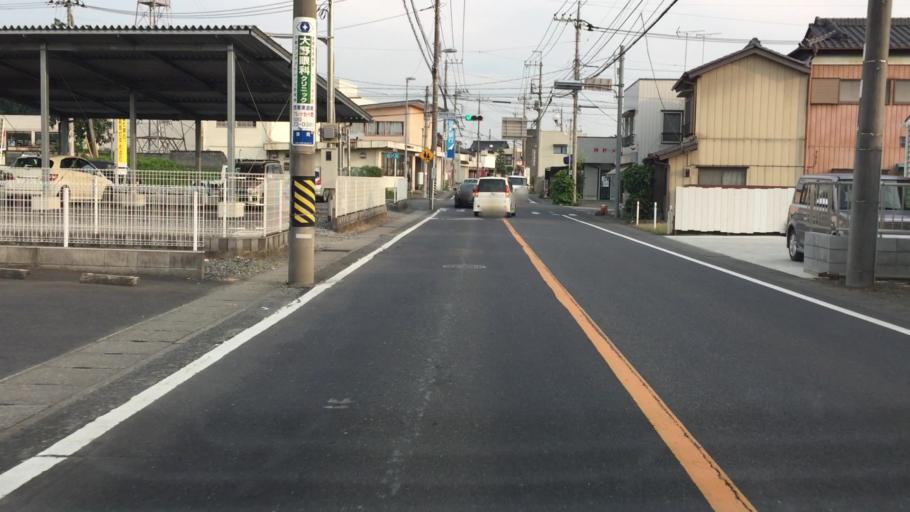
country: JP
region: Tochigi
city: Fujioka
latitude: 36.2610
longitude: 139.6500
